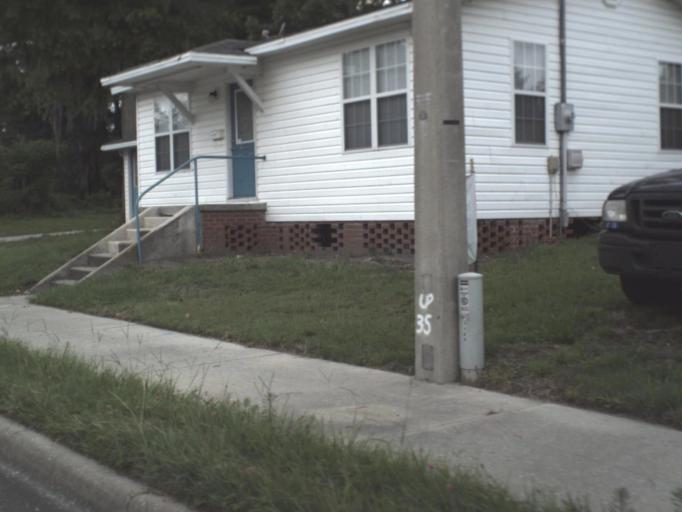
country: US
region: Florida
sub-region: Columbia County
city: Lake City
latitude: 30.1834
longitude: -82.6274
